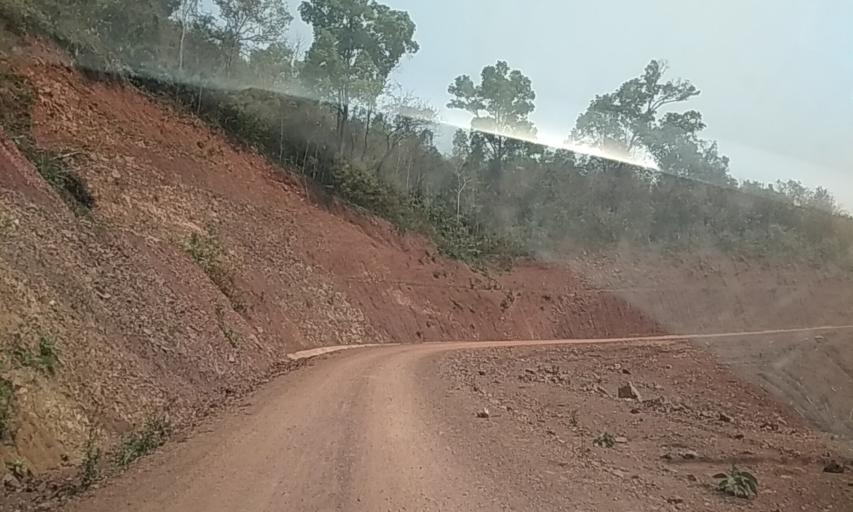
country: VN
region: Huyen Dien Bien
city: Dien Bien Phu
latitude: 21.4522
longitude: 102.7666
